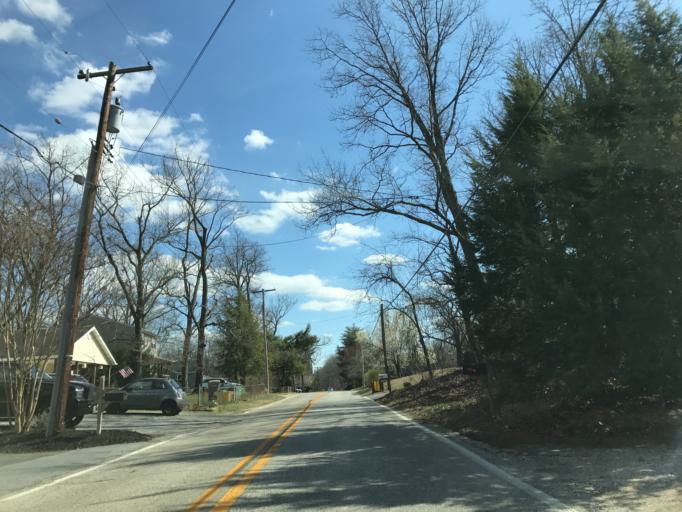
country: US
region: Maryland
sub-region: Anne Arundel County
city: Pasadena
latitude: 39.1289
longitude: -76.5767
